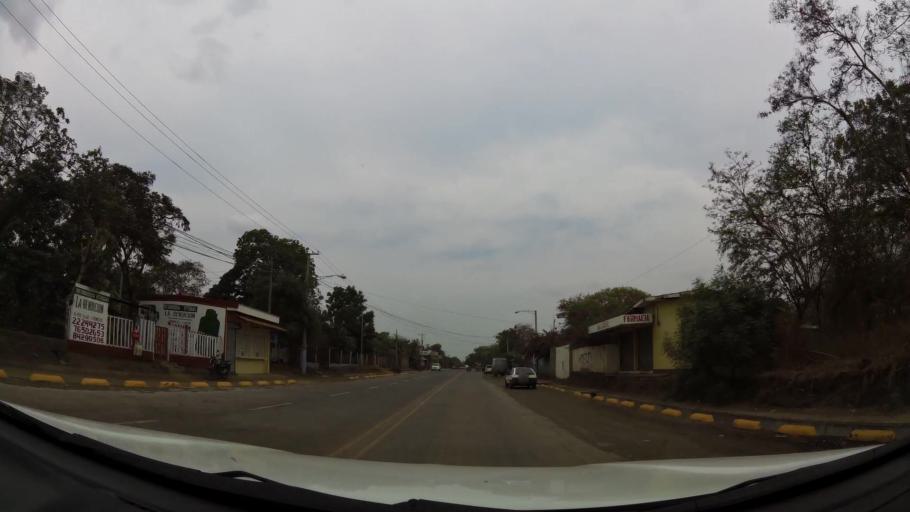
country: NI
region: Managua
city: Managua
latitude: 12.1228
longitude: -86.1715
